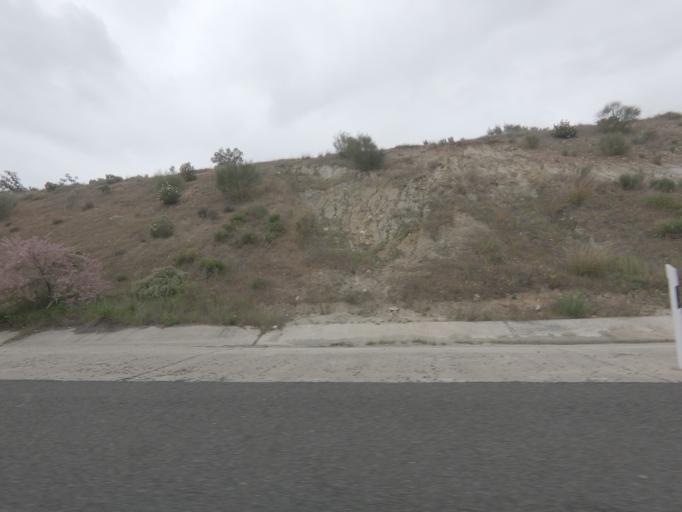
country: ES
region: Extremadura
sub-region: Provincia de Caceres
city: Jarilla
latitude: 40.1976
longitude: -5.9985
